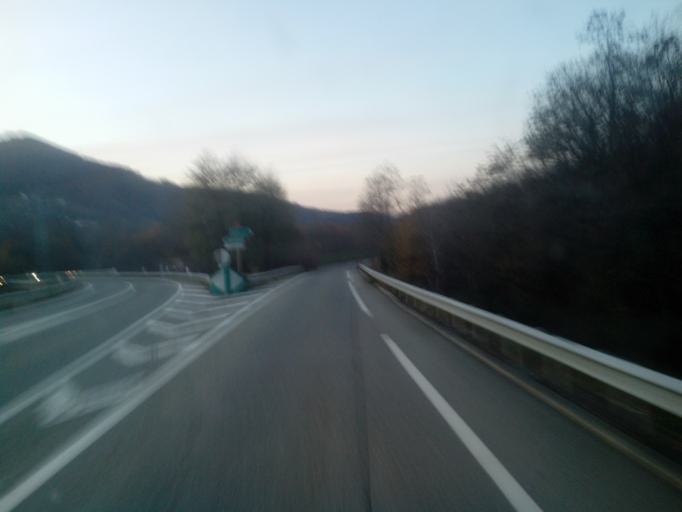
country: FR
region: Midi-Pyrenees
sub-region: Departement de l'Ariege
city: Montgaillard
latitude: 42.9220
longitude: 1.6374
